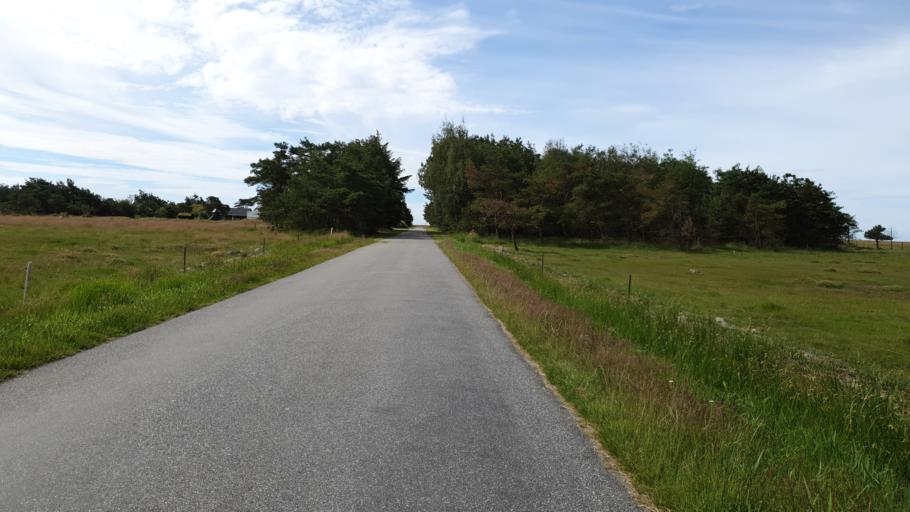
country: DK
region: North Denmark
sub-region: Laeso Kommune
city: Byrum
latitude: 57.2422
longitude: 10.9899
